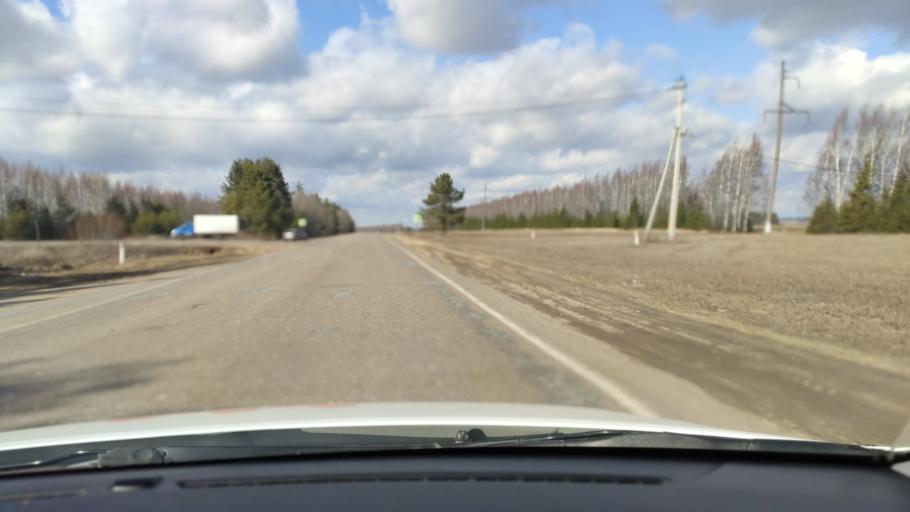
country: RU
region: Tatarstan
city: Vysokaya Gora
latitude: 56.0656
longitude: 49.2012
